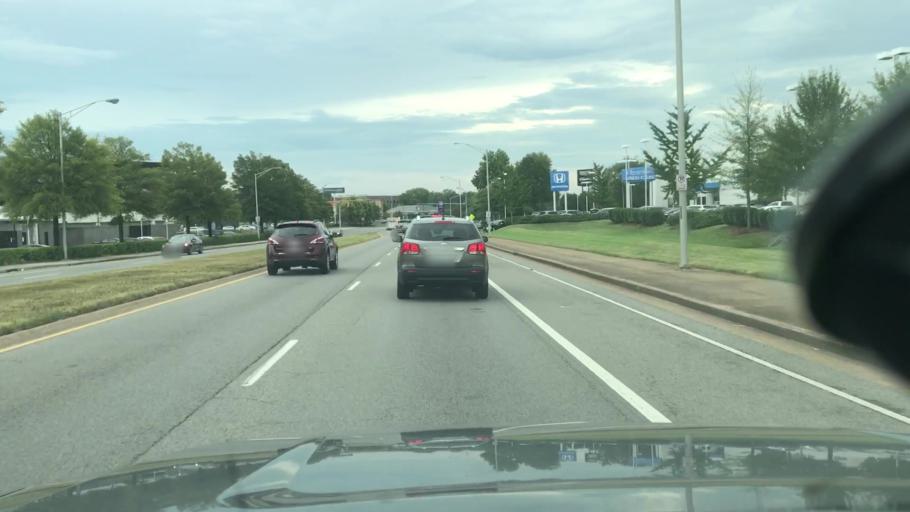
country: US
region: Tennessee
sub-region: Davidson County
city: Nashville
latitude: 36.1973
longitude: -86.8312
